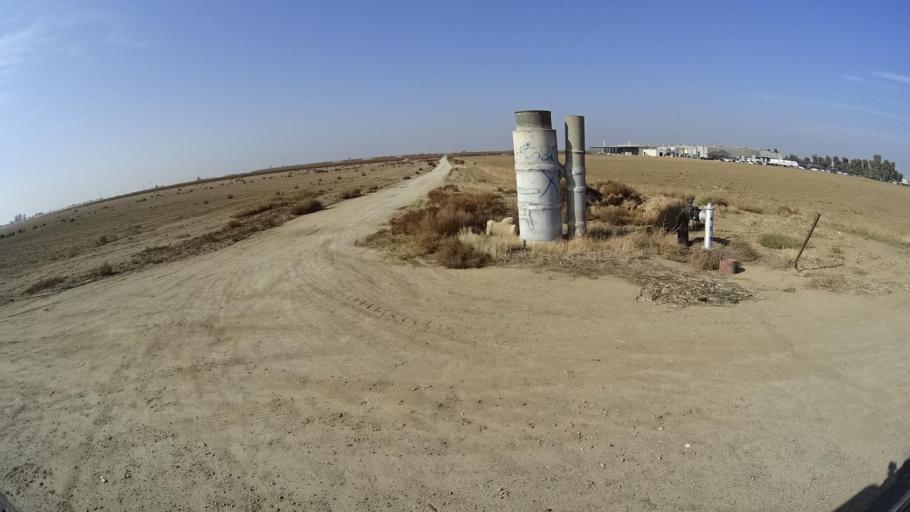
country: US
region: California
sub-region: Kern County
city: McFarland
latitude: 35.7000
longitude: -119.2230
